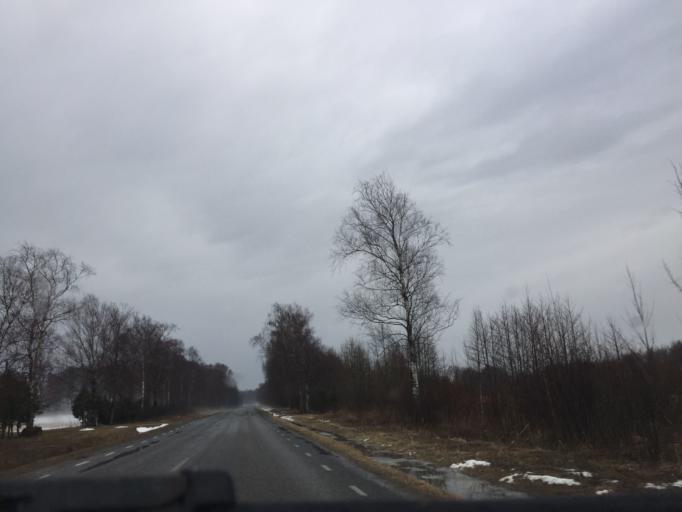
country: EE
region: Saare
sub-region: Orissaare vald
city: Orissaare
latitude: 58.5717
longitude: 23.0325
